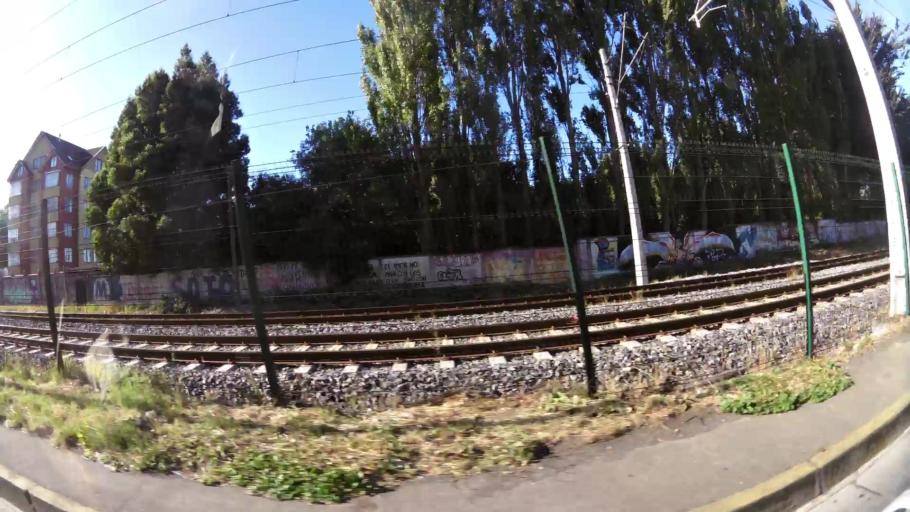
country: CL
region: Biobio
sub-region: Provincia de Concepcion
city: Concepcion
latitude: -36.8378
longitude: -73.1118
